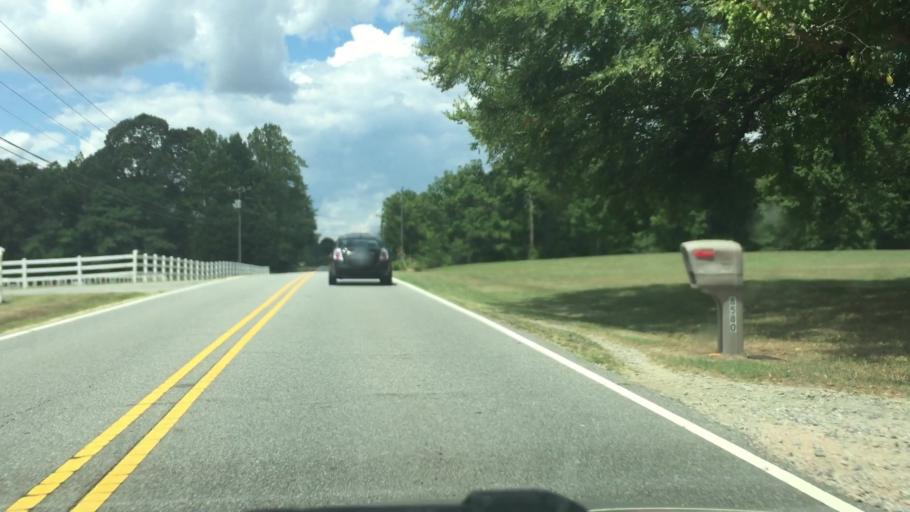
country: US
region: North Carolina
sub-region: Rowan County
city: Enochville
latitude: 35.4809
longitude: -80.7214
